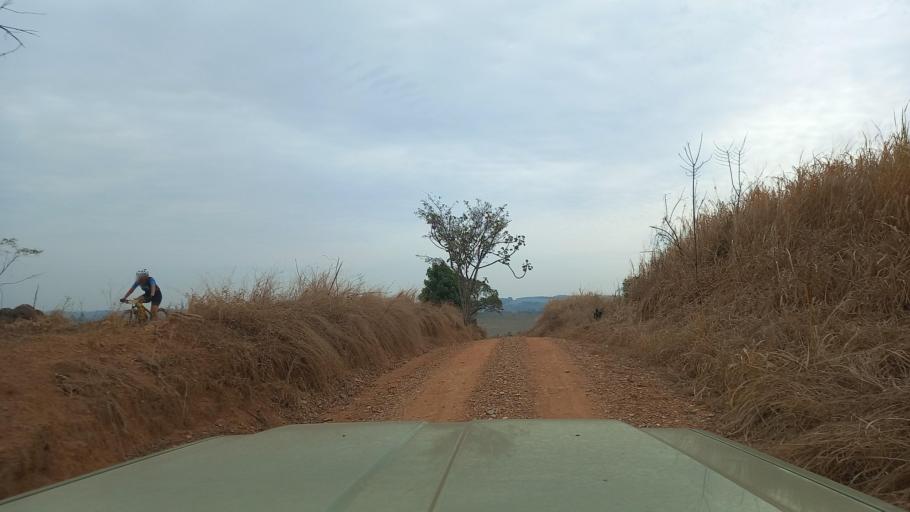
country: BR
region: Sao Paulo
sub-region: Moji-Guacu
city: Mogi-Gaucu
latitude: -22.2789
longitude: -46.8308
